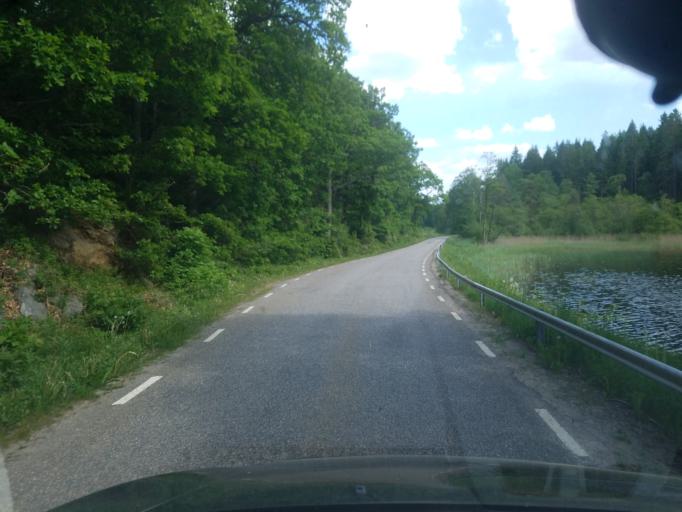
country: SE
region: Vaestra Goetaland
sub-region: Stenungsunds Kommun
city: Stora Hoga
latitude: 57.9982
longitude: 11.9404
